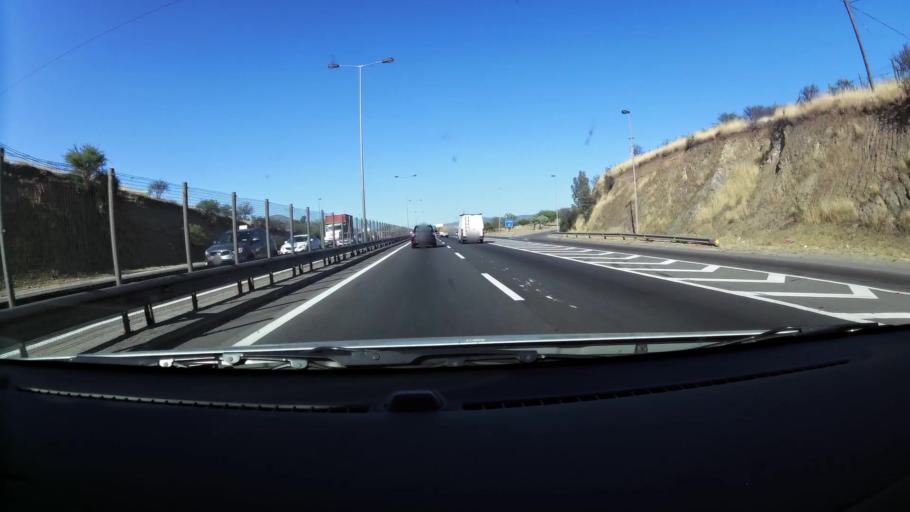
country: CL
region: Santiago Metropolitan
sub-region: Provincia de Santiago
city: Lo Prado
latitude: -33.4386
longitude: -70.8315
